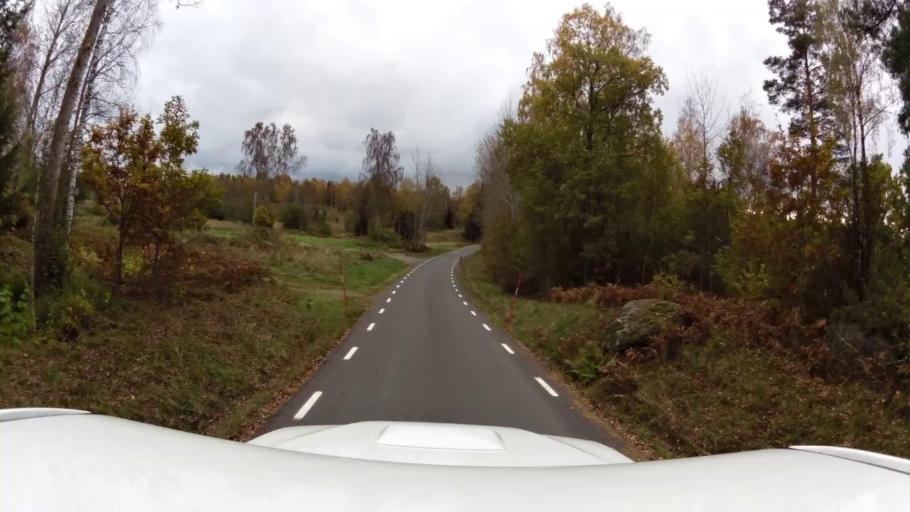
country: SE
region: OEstergoetland
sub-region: Linkopings Kommun
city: Ljungsbro
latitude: 58.5768
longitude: 15.4624
